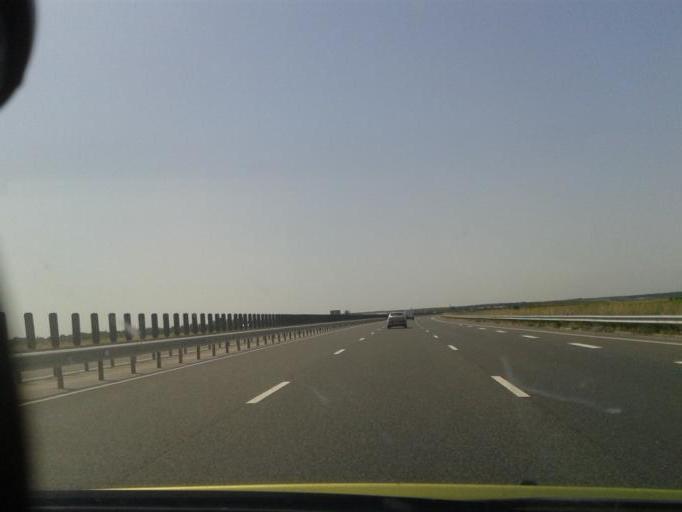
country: RO
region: Ilfov
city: Stefanestii de Jos
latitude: 44.5508
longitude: 26.1833
